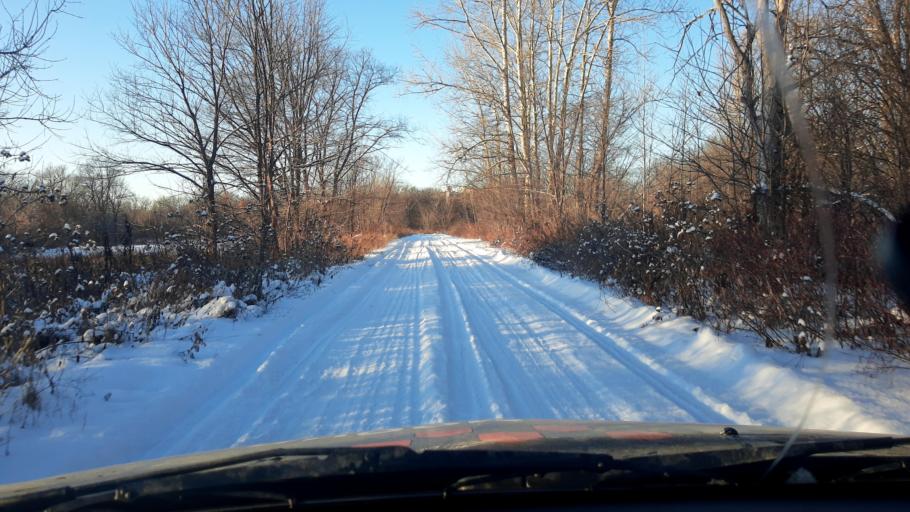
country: RU
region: Bashkortostan
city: Ufa
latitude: 54.6618
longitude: 55.9618
